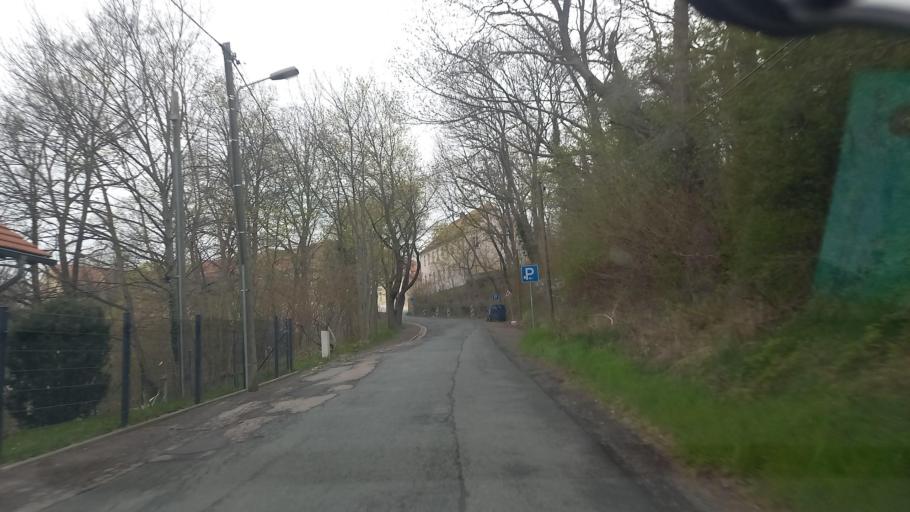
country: DE
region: Saxony
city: Wilkau-Hasslau
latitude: 50.6848
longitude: 12.4743
